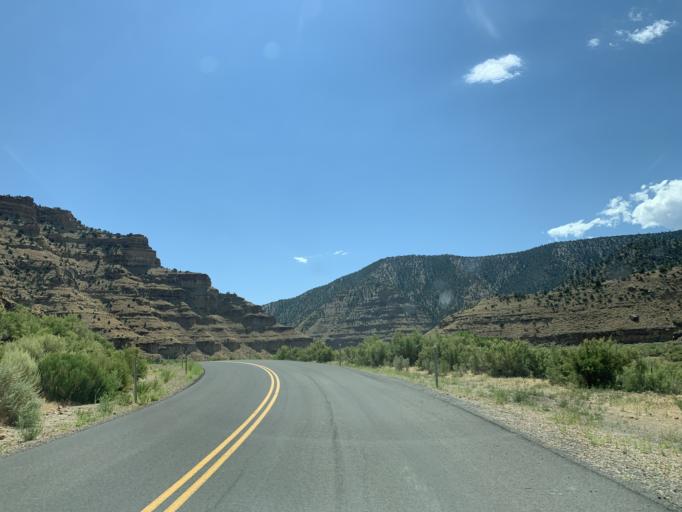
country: US
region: Utah
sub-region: Carbon County
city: East Carbon City
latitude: 39.8132
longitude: -110.2798
